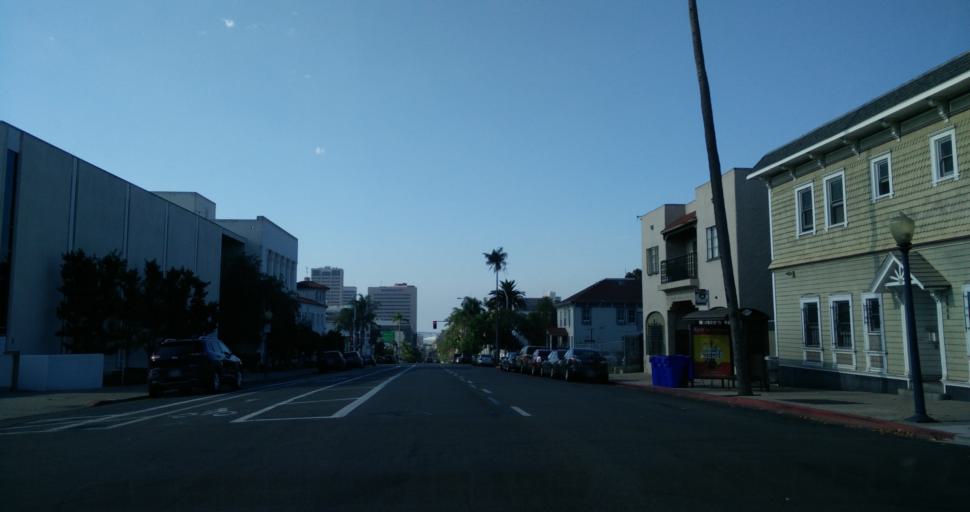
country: US
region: California
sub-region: San Diego County
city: San Diego
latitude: 32.7272
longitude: -117.1612
